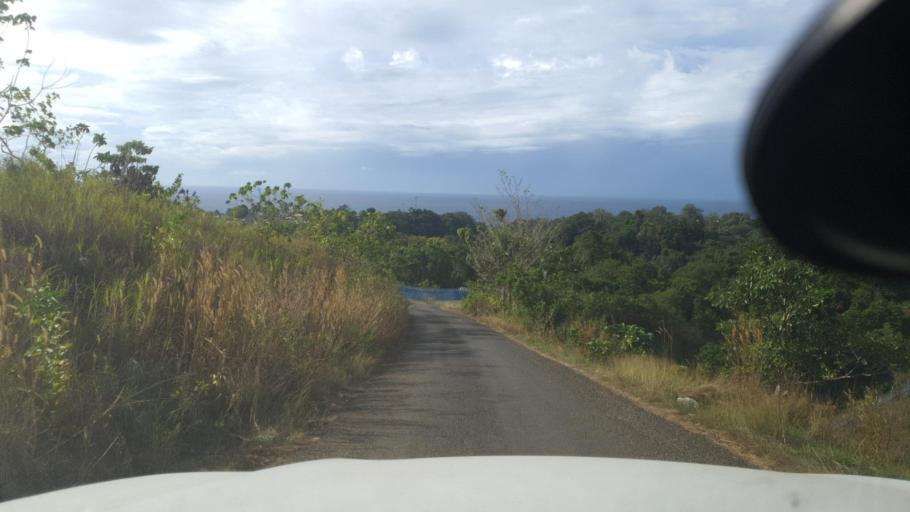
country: SB
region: Guadalcanal
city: Honiara
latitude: -9.4421
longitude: 159.9376
